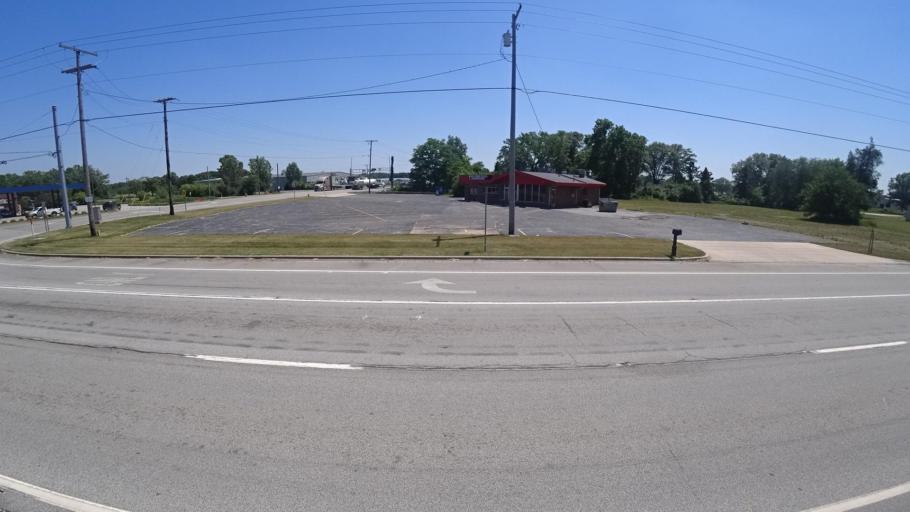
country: US
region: Indiana
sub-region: Porter County
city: Burns Harbor
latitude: 41.6014
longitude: -87.1255
